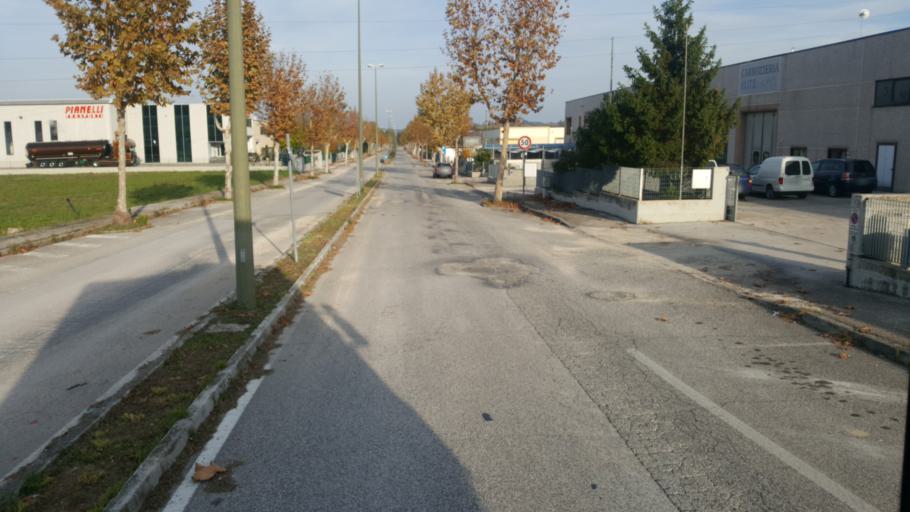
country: IT
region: The Marches
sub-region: Provincia di Ancona
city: Casine
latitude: 43.6448
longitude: 13.1379
